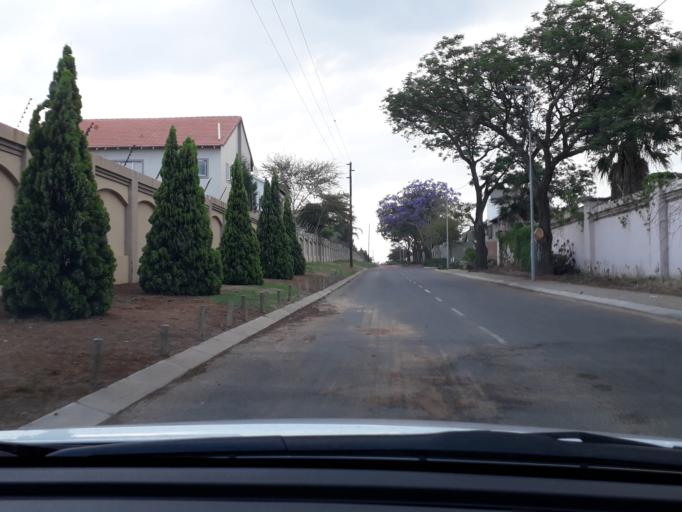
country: ZA
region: Gauteng
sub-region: City of Johannesburg Metropolitan Municipality
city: Diepsloot
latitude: -25.9955
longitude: 27.9948
